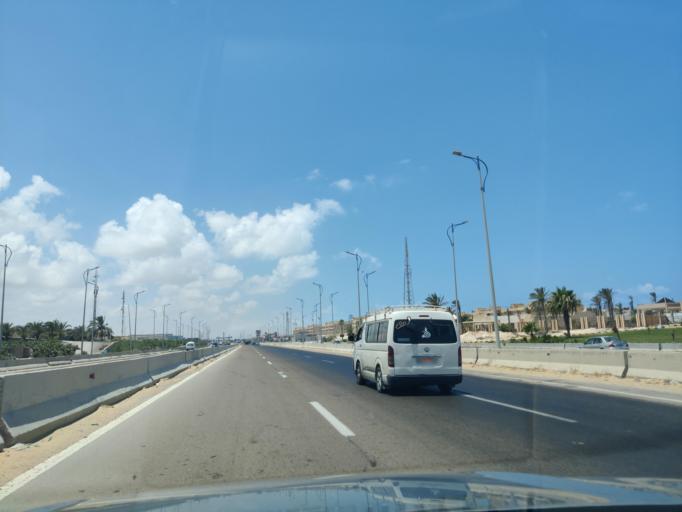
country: EG
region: Muhafazat Matruh
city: Al `Alamayn
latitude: 30.9021
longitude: 29.4180
